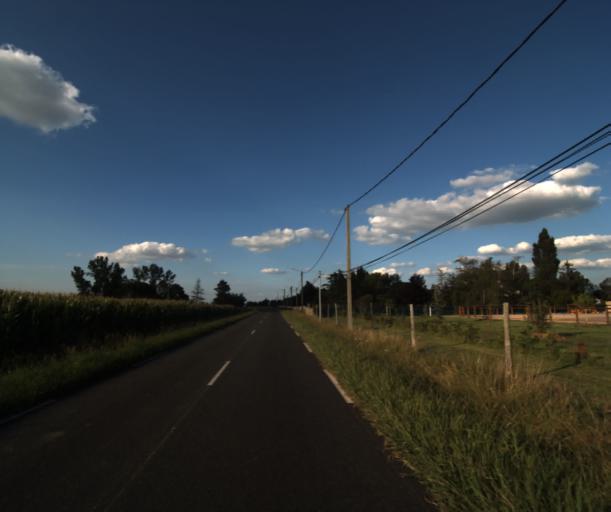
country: FR
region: Midi-Pyrenees
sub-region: Departement de la Haute-Garonne
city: Labastidette
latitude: 43.4710
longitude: 1.2547
